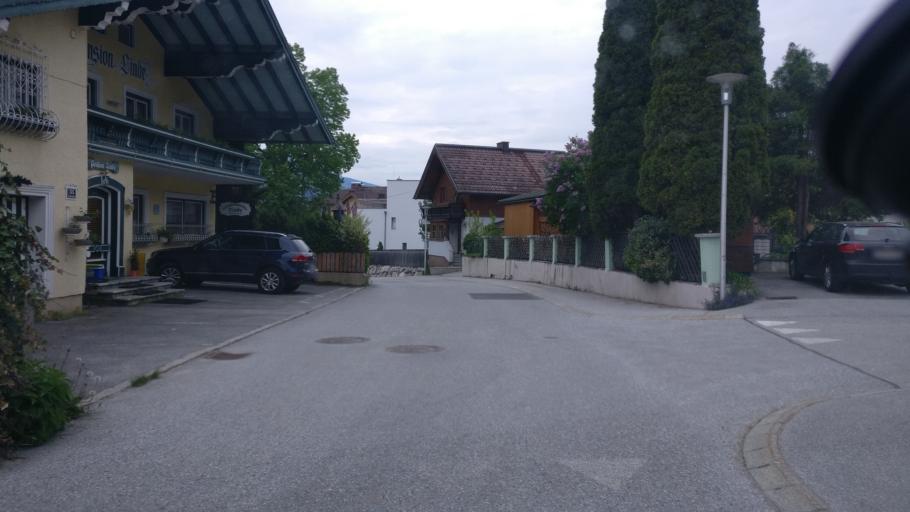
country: AT
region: Salzburg
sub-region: Politischer Bezirk Sankt Johann im Pongau
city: Radstadt
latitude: 47.3842
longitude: 13.4511
